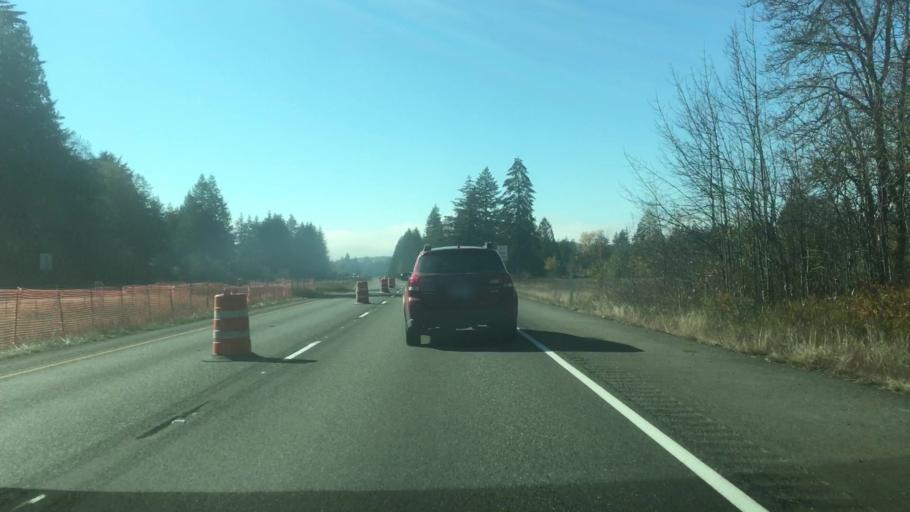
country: US
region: Washington
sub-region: Grays Harbor County
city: McCleary
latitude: 47.0538
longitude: -123.2895
